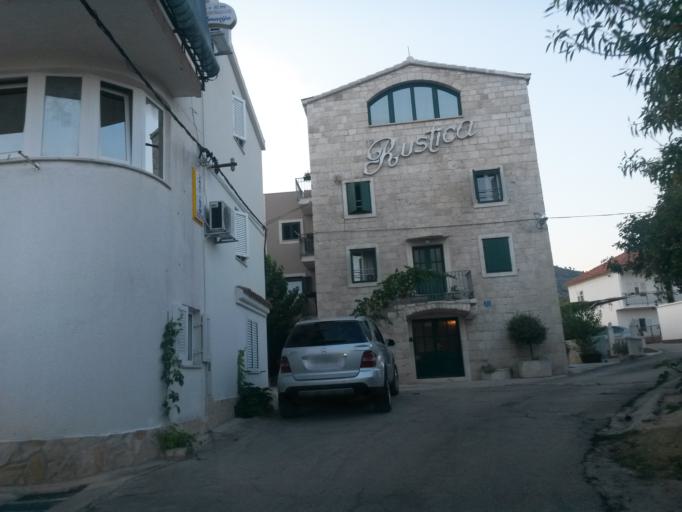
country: HR
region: Splitsko-Dalmatinska
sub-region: Grad Trogir
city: Trogir
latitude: 43.5127
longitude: 16.1836
